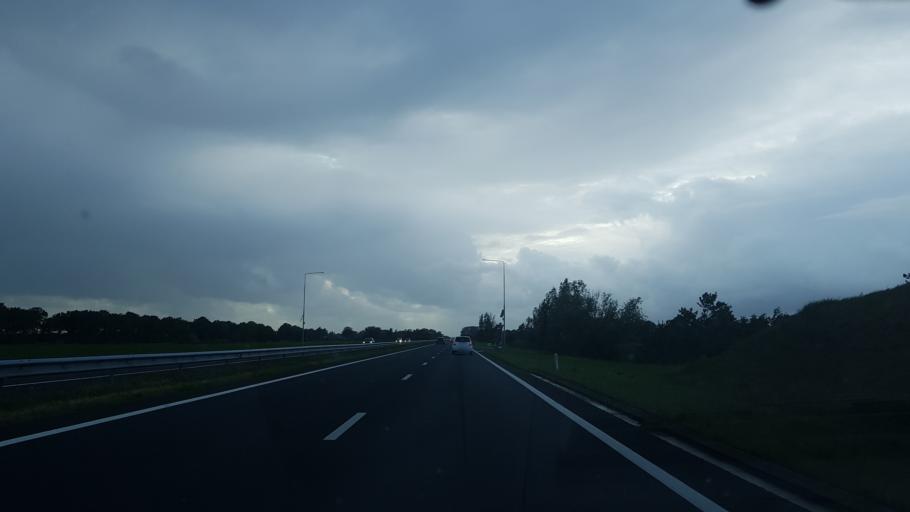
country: NL
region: Friesland
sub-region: Gemeente Smallingerland
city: Oudega
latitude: 53.1483
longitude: 5.9860
